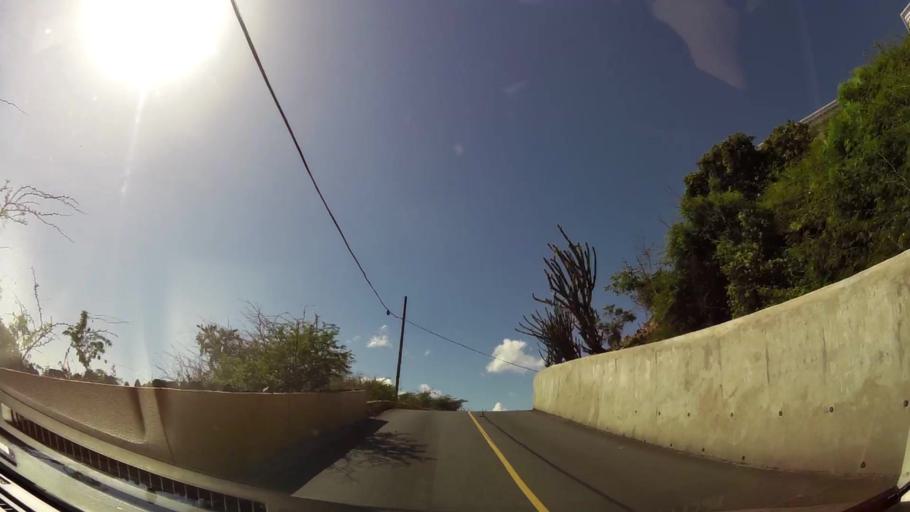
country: VG
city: Tortola
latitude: 18.4138
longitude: -64.5937
